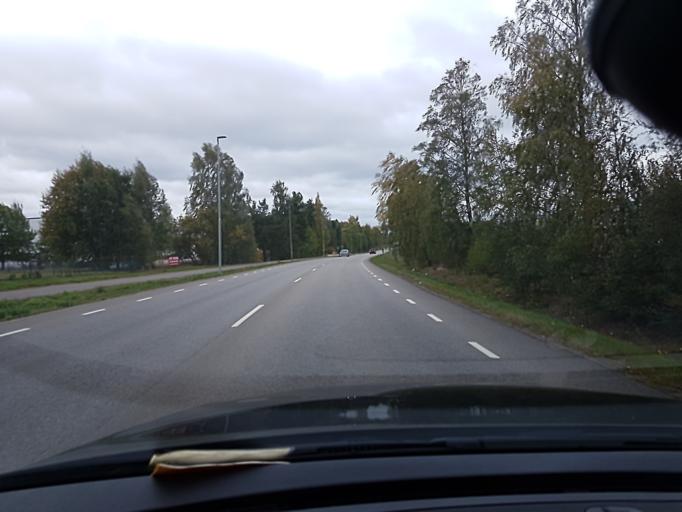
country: SE
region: Kronoberg
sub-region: Vaxjo Kommun
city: Vaexjoe
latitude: 56.9051
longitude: 14.8235
